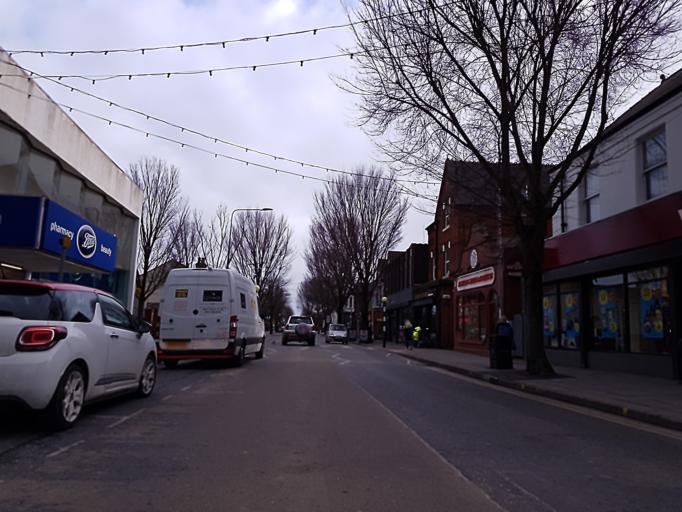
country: GB
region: England
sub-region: North East Lincolnshire
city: Cleethorpes
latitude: 53.5591
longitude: -0.0314
